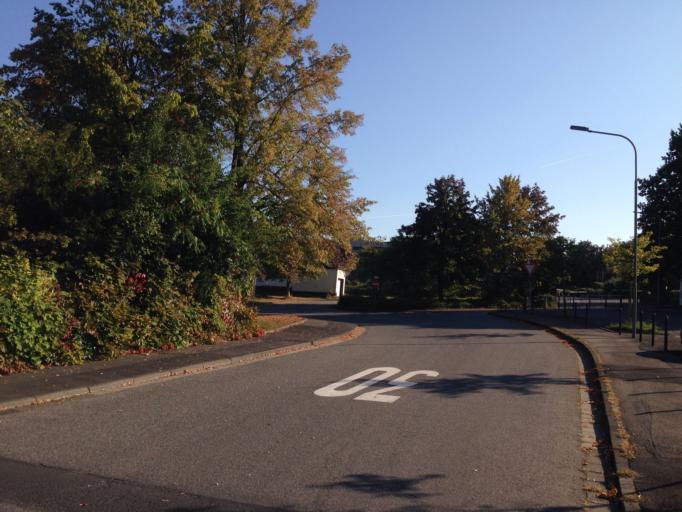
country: DE
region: Hesse
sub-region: Regierungsbezirk Giessen
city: Giessen
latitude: 50.5404
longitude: 8.7262
